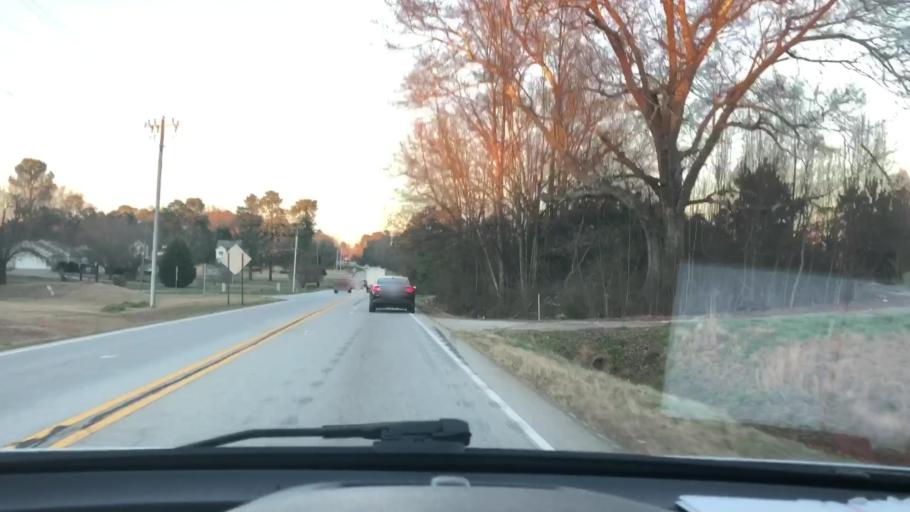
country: US
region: Georgia
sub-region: Barrow County
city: Winder
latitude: 33.9283
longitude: -83.7693
